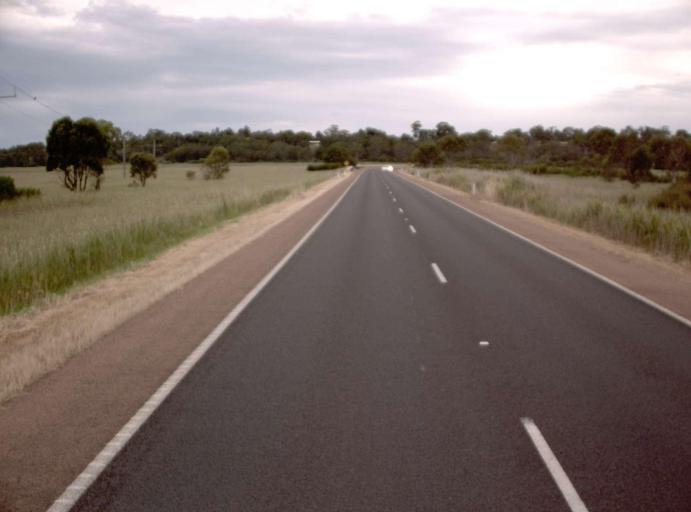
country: AU
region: Victoria
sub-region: East Gippsland
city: Bairnsdale
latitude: -37.8822
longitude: 147.6576
